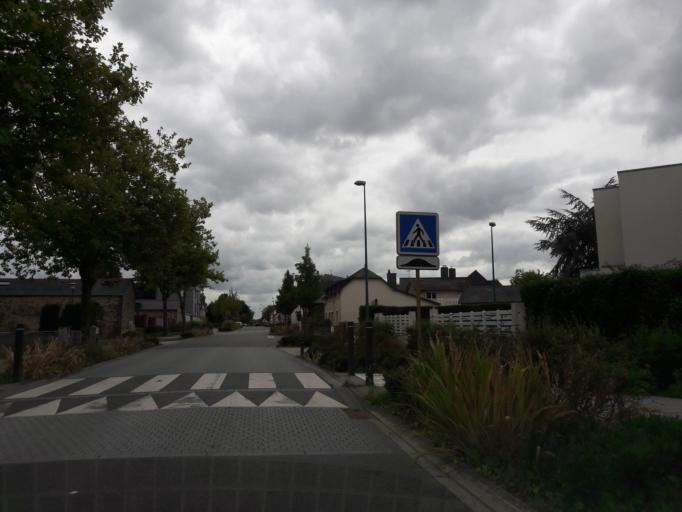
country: FR
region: Brittany
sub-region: Departement d'Ille-et-Vilaine
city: Chartres-de-Bretagne
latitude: 48.0157
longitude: -1.7040
